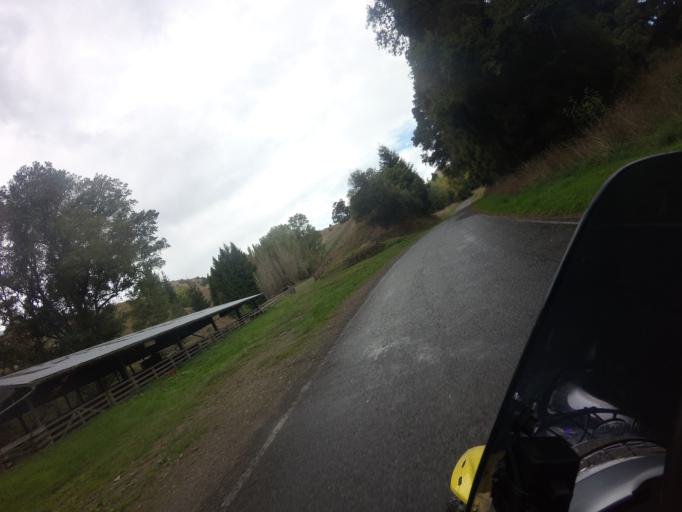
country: NZ
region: Gisborne
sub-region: Gisborne District
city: Gisborne
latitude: -38.6269
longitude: 177.6591
